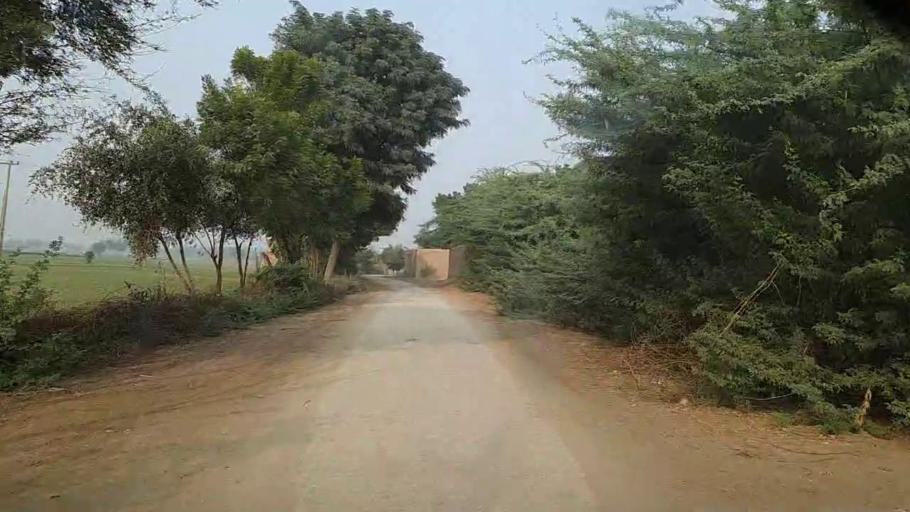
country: PK
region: Sindh
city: Bozdar
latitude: 27.1391
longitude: 68.6625
